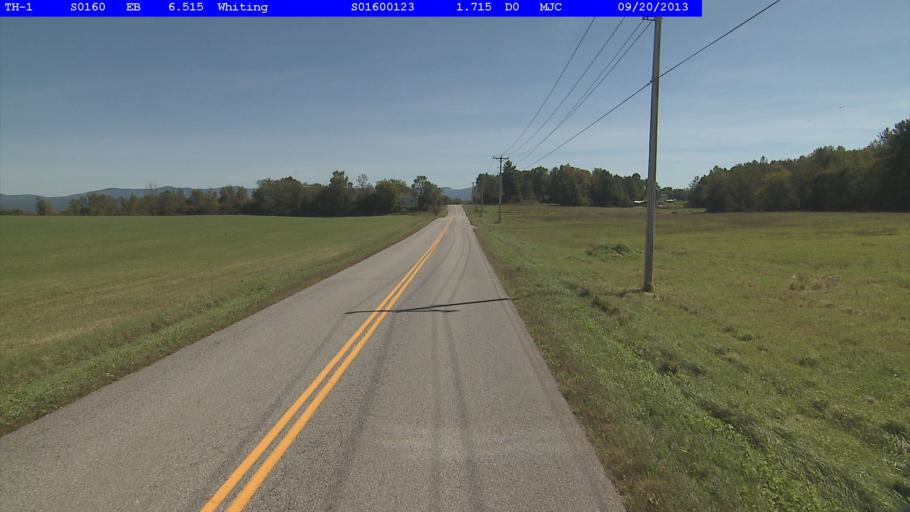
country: US
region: Vermont
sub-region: Rutland County
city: Brandon
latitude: 43.8614
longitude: -73.1921
